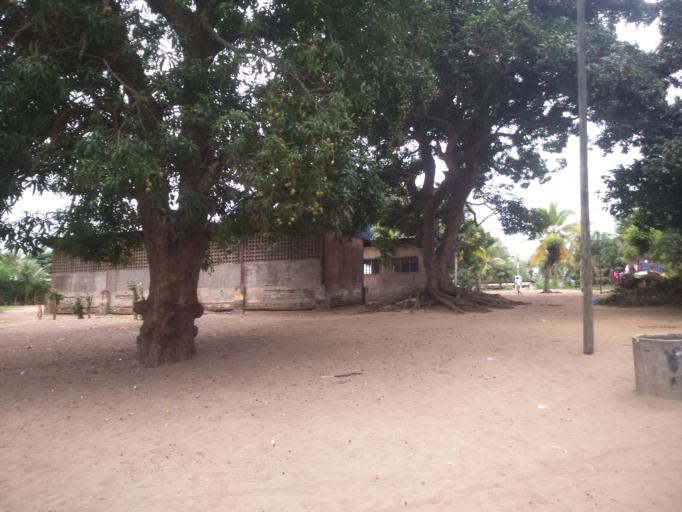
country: CI
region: Lagunes
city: Bingerville
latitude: 5.3301
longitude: -3.8959
